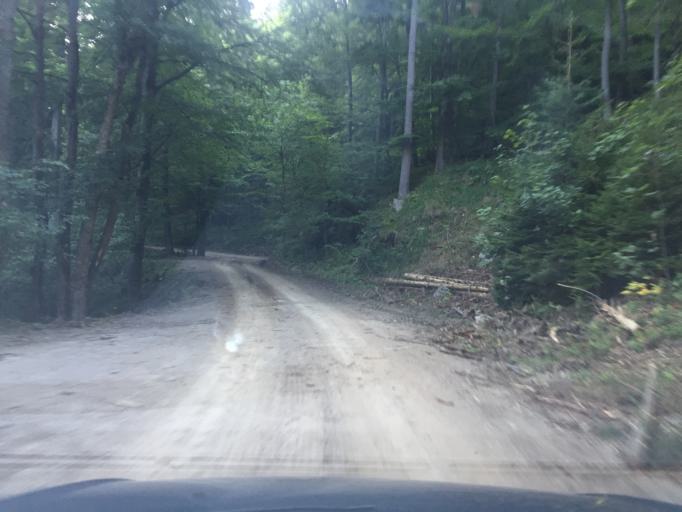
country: SI
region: Ravne na Koroskem
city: Kotlje
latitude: 46.4741
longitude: 14.9779
